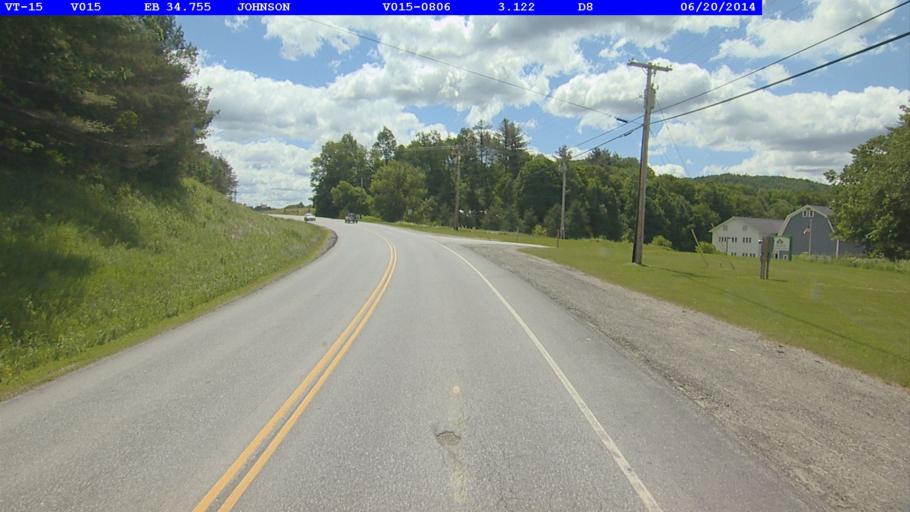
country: US
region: Vermont
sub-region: Lamoille County
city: Johnson
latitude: 44.6372
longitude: -72.6979
